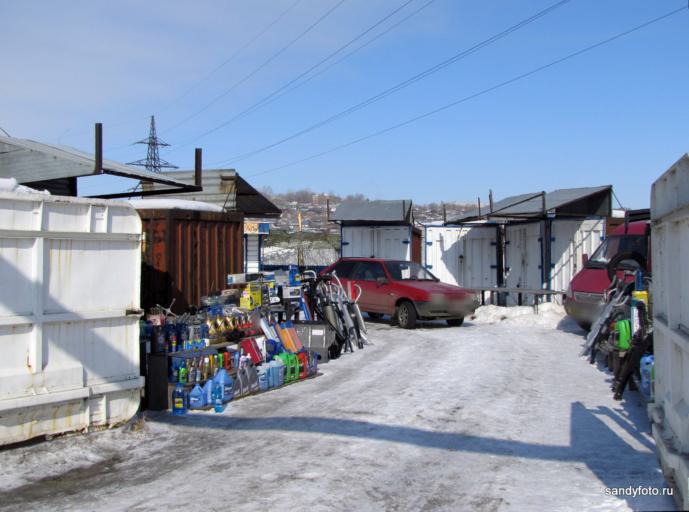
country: RU
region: Chelyabinsk
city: Troitsk
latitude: 54.0924
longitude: 61.5562
